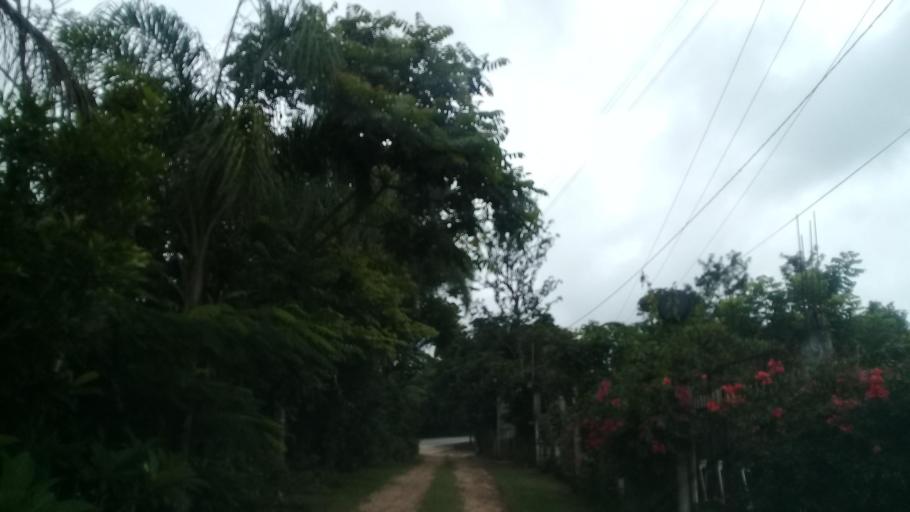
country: MX
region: Veracruz
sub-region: Emiliano Zapata
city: Jacarandas
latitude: 19.4783
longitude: -96.8575
